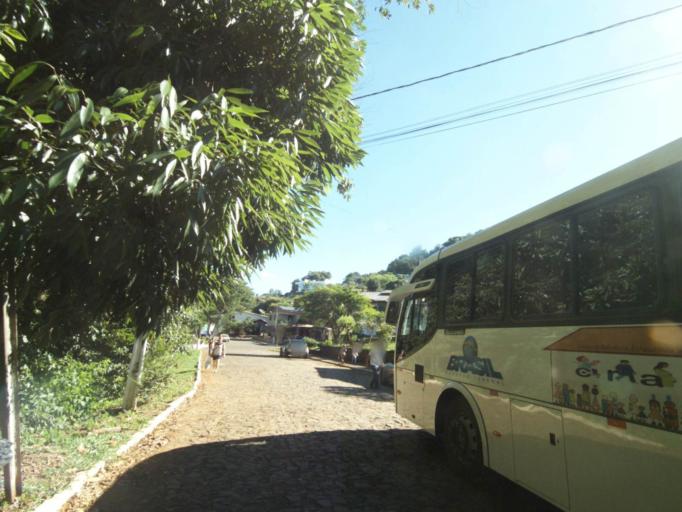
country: BR
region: Parana
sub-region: Ampere
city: Ampere
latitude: -26.1722
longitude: -53.3638
